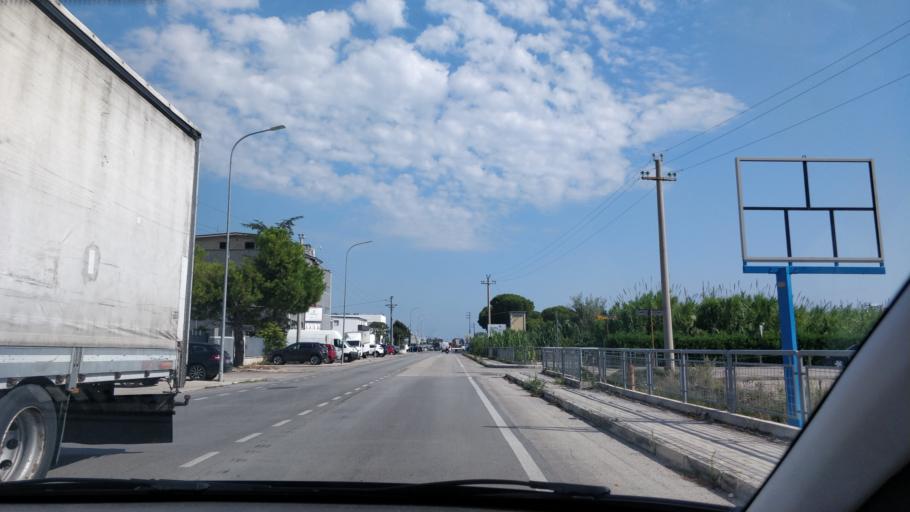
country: IT
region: Abruzzo
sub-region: Provincia di Pescara
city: Santa Teresa
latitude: 42.4101
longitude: 14.1663
